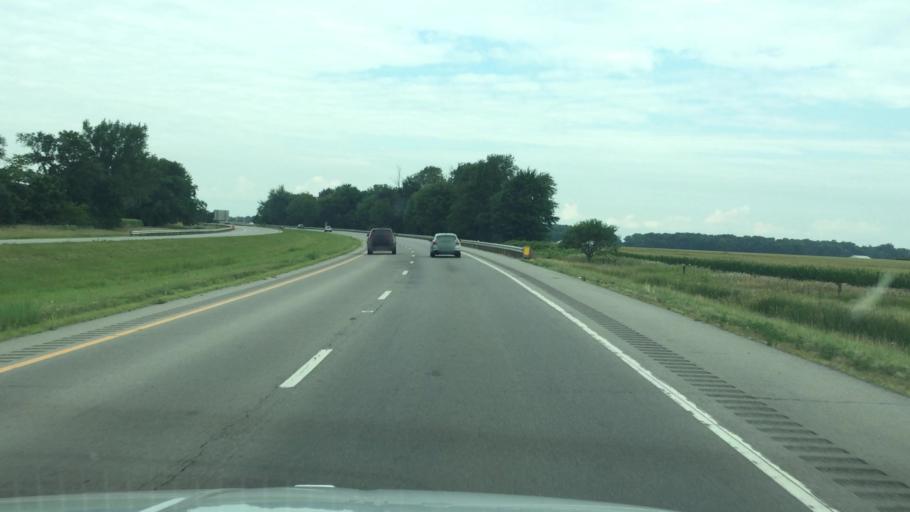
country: US
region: Ohio
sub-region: Wyandot County
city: Carey
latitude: 40.9806
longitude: -83.4971
